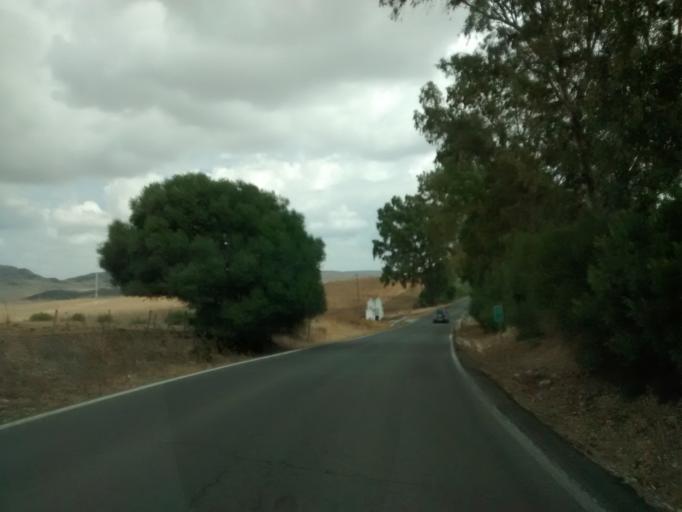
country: ES
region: Andalusia
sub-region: Provincia de Cadiz
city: Paterna de Rivera
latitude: 36.4976
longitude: -5.8893
